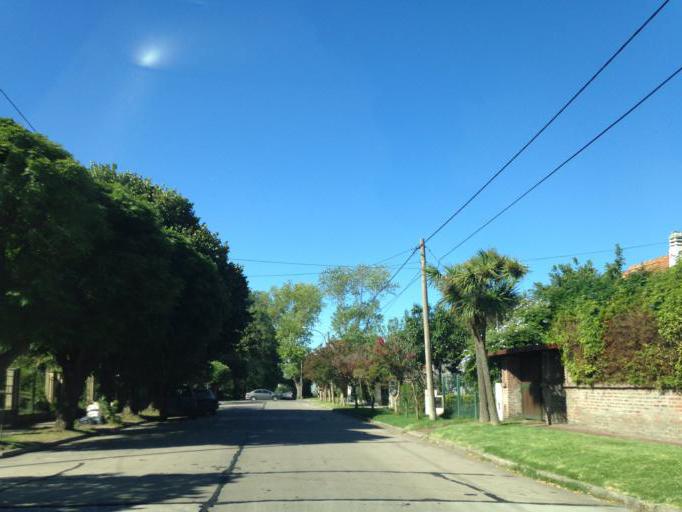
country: AR
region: Buenos Aires
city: Mar del Plata
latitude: -38.0276
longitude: -57.5442
